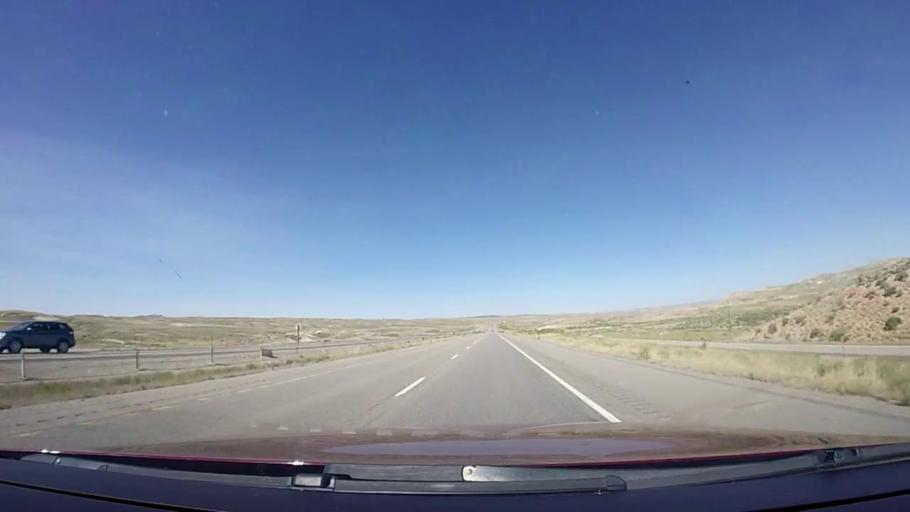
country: US
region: Wyoming
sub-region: Sweetwater County
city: Rock Springs
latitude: 41.6474
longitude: -108.6770
